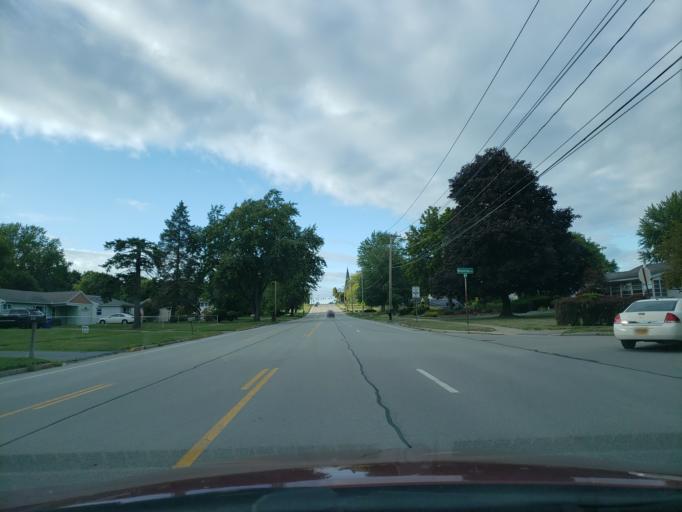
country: US
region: New York
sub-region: Monroe County
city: Greece
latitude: 43.2487
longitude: -77.6592
